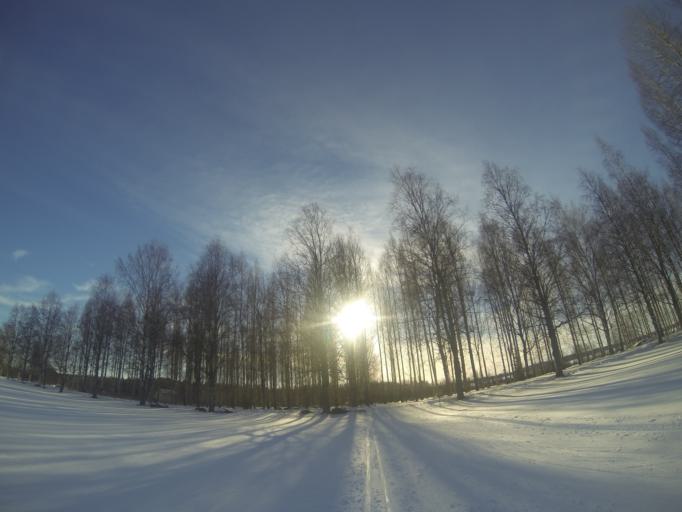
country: FI
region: Southern Savonia
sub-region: Savonlinna
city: Savonlinna
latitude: 61.8982
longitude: 28.9172
